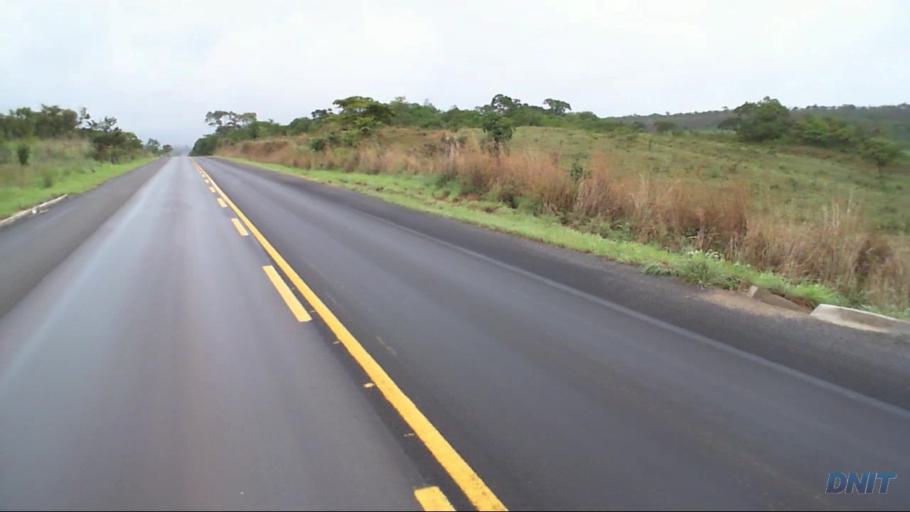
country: BR
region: Goias
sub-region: Padre Bernardo
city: Padre Bernardo
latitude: -15.2016
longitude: -48.4550
